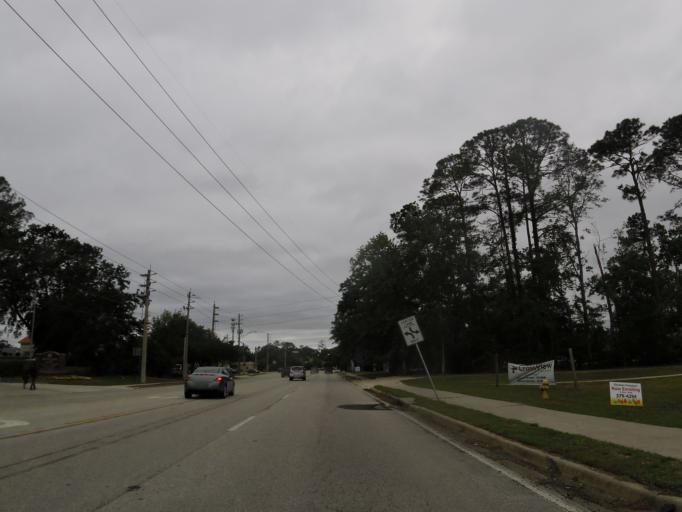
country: US
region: Florida
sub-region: Saint Johns County
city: Fruit Cove
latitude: 30.1823
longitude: -81.6070
